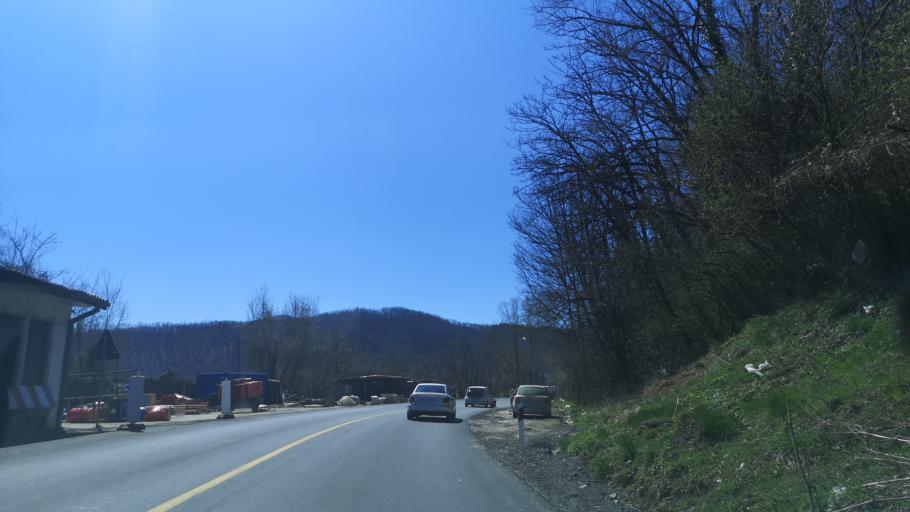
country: RS
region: Central Serbia
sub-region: Moravicki Okrug
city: Lucani
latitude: 43.8714
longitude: 20.1166
